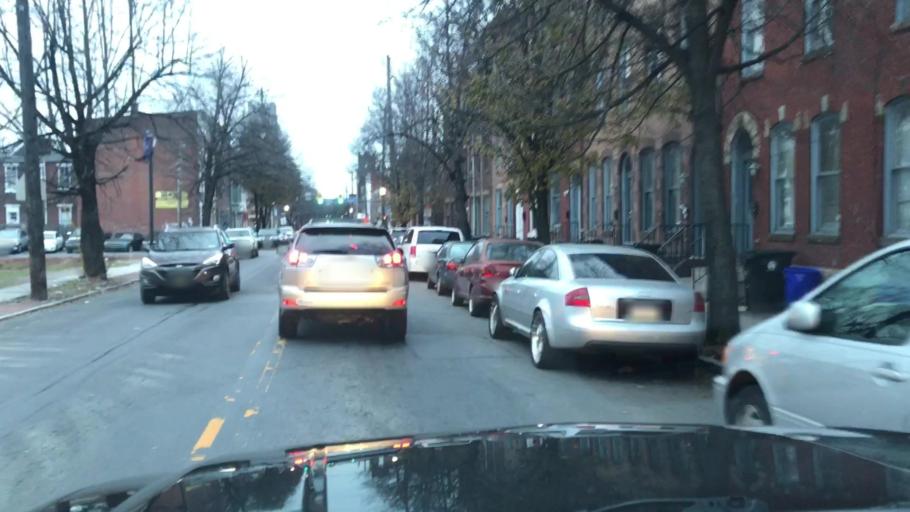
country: US
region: Pennsylvania
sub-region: Dauphin County
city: Harrisburg
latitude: 40.2621
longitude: -76.8683
